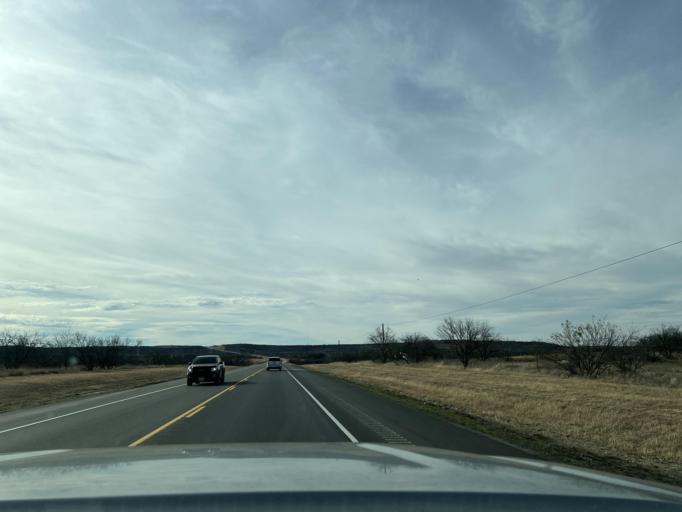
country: US
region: Texas
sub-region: Shackelford County
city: Albany
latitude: 32.7134
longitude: -99.3457
